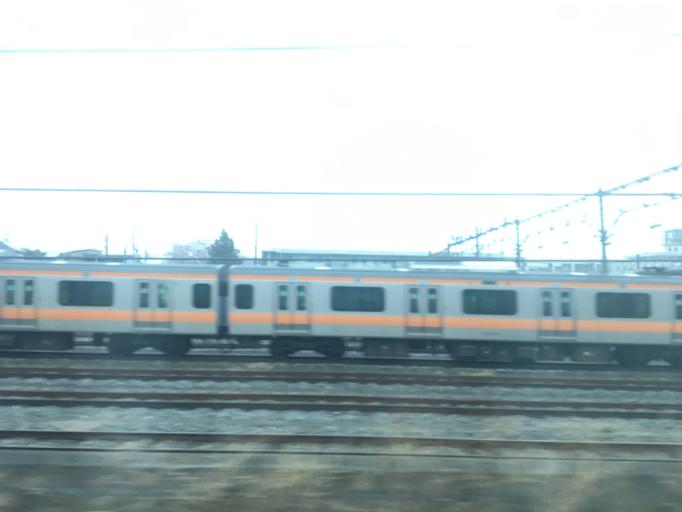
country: JP
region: Tokyo
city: Hino
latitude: 35.6541
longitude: 139.3728
